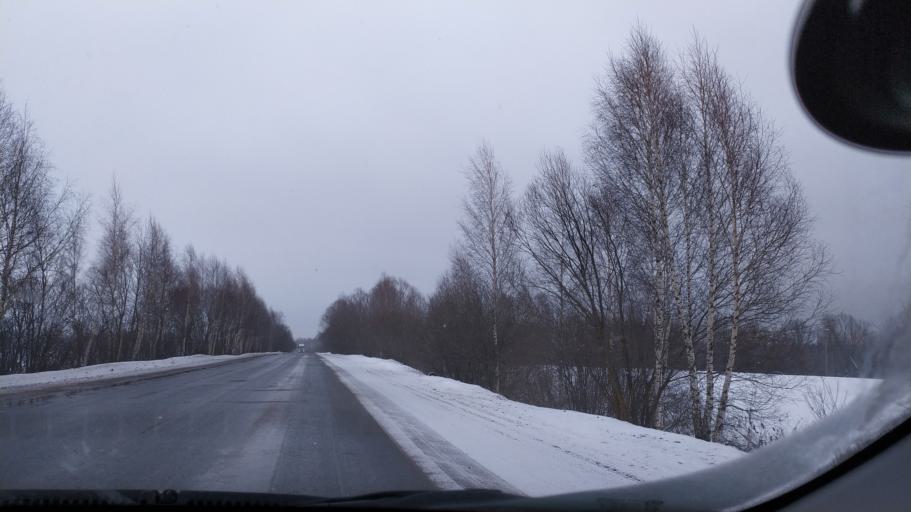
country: RU
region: Mariy-El
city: Krasnogorskiy
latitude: 56.1513
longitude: 48.1484
